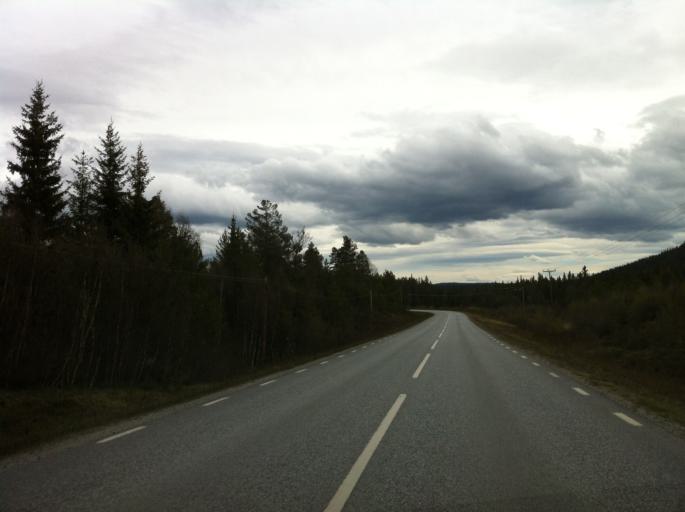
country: SE
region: Jaemtland
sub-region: Are Kommun
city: Are
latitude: 62.5984
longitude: 12.5303
